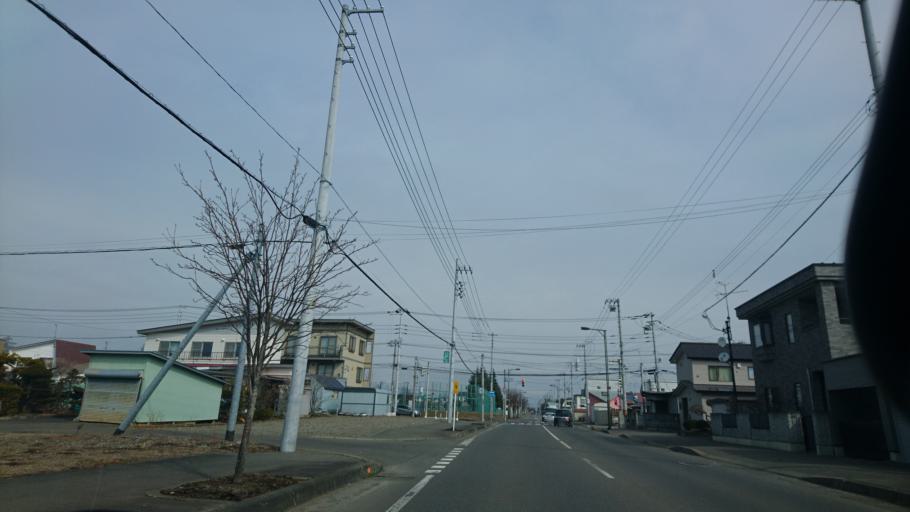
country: JP
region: Hokkaido
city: Otofuke
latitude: 42.9672
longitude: 143.2130
